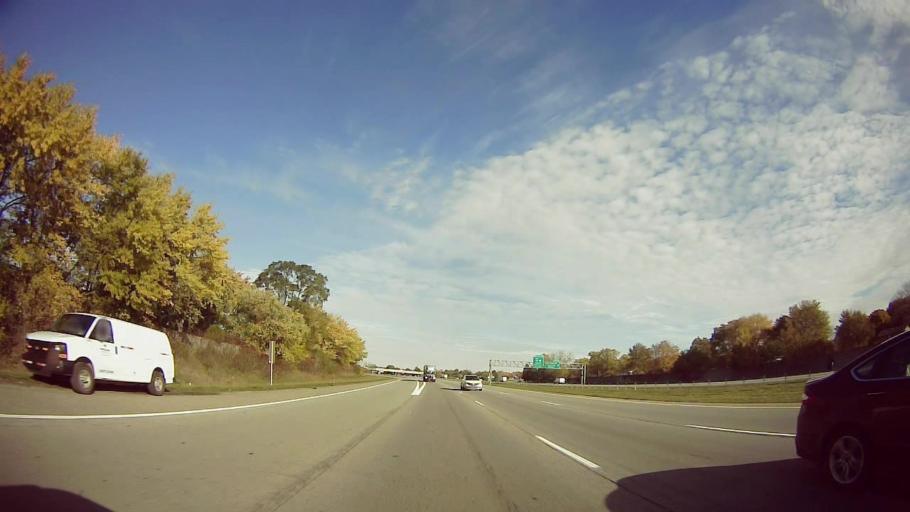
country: US
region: Michigan
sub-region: Wayne County
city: Plymouth
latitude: 42.3540
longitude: -83.4370
